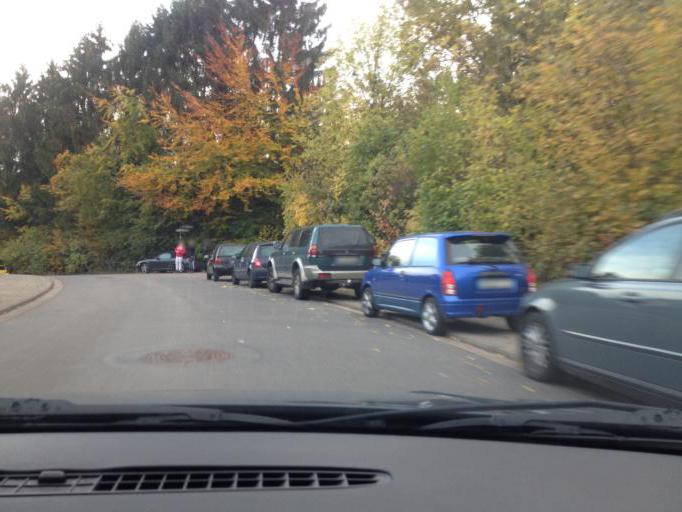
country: DE
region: Saarland
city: Ottweiler
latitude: 49.4042
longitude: 7.1472
